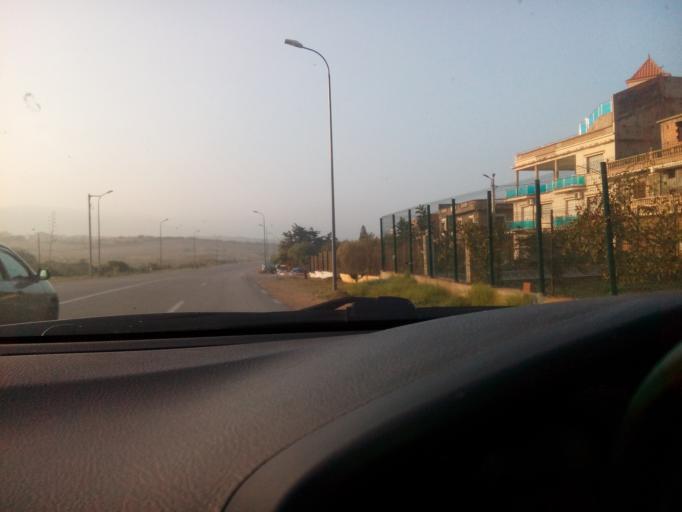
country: DZ
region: Oran
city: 'Ain el Turk
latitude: 35.7300
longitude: -0.8422
